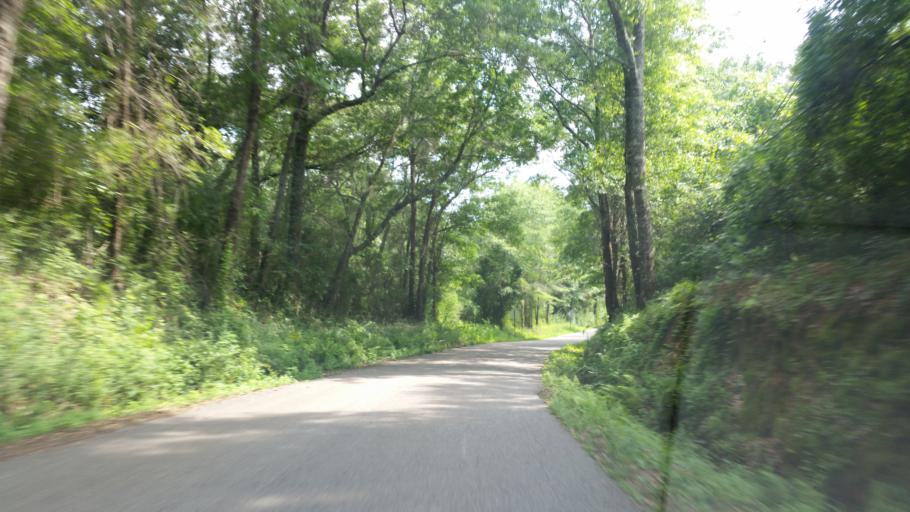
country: US
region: Florida
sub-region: Escambia County
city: Cantonment
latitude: 30.6307
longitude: -87.3817
